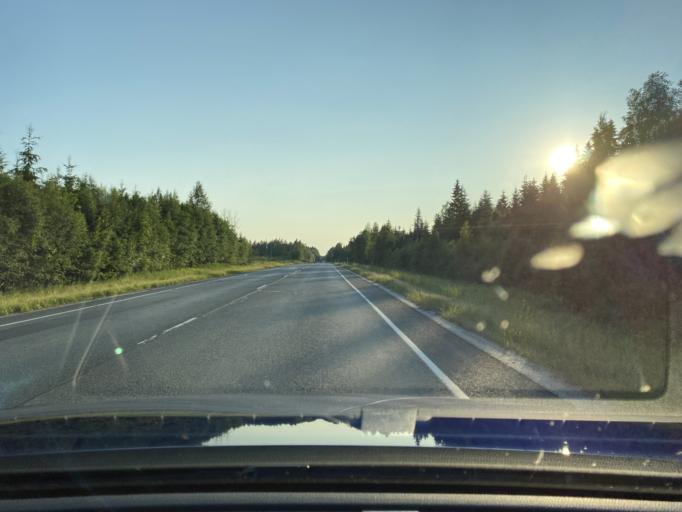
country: FI
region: Haeme
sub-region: Forssa
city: Tammela
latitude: 60.8258
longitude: 23.9570
